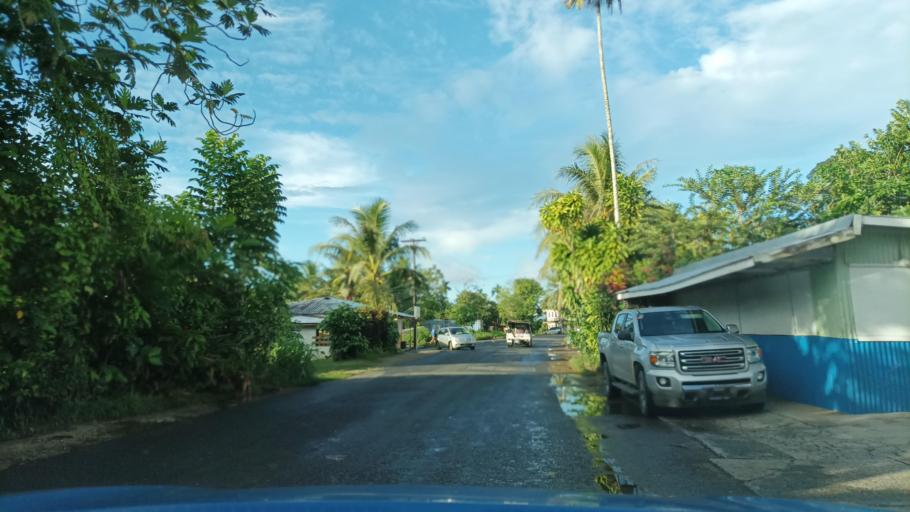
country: FM
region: Pohnpei
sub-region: Kolonia Municipality
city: Kolonia
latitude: 6.9603
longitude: 158.2087
